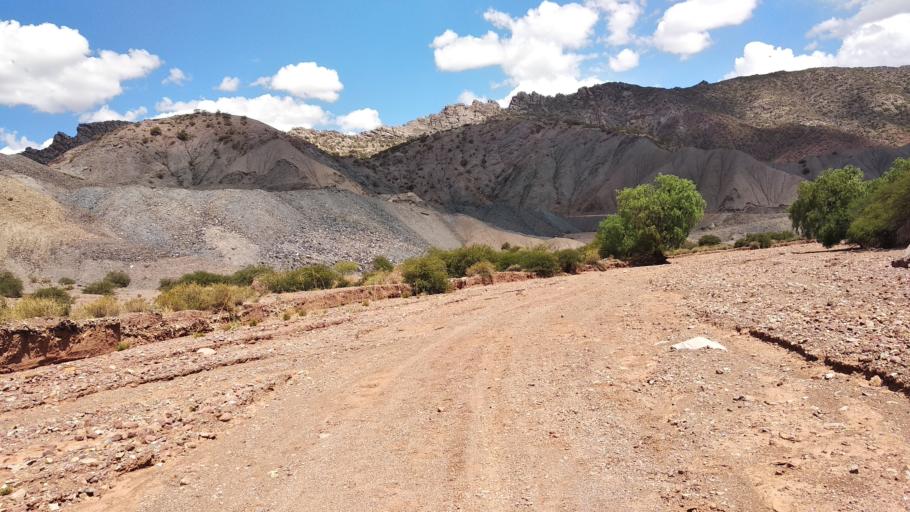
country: BO
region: Potosi
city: Tupiza
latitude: -21.4823
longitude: -65.7305
